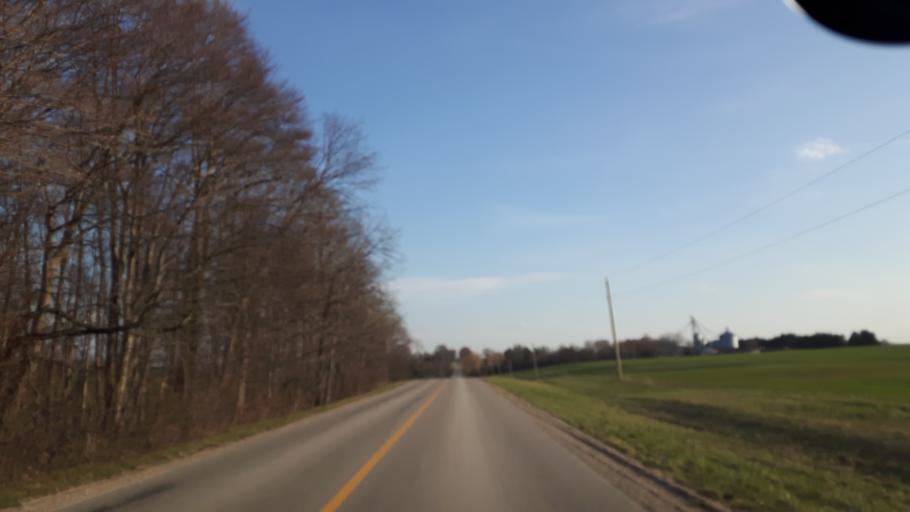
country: CA
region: Ontario
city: Goderich
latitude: 43.6487
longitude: -81.6643
